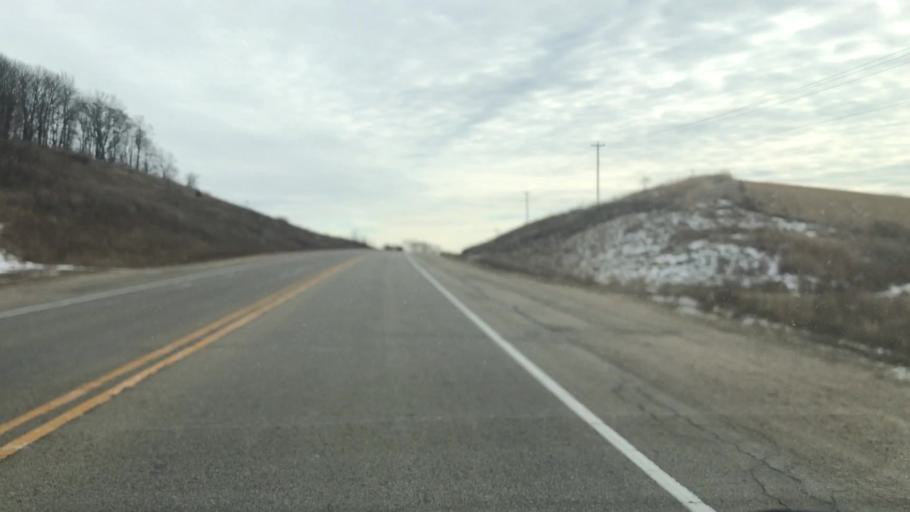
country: US
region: Wisconsin
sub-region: Dodge County
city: Theresa
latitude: 43.4332
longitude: -88.4589
